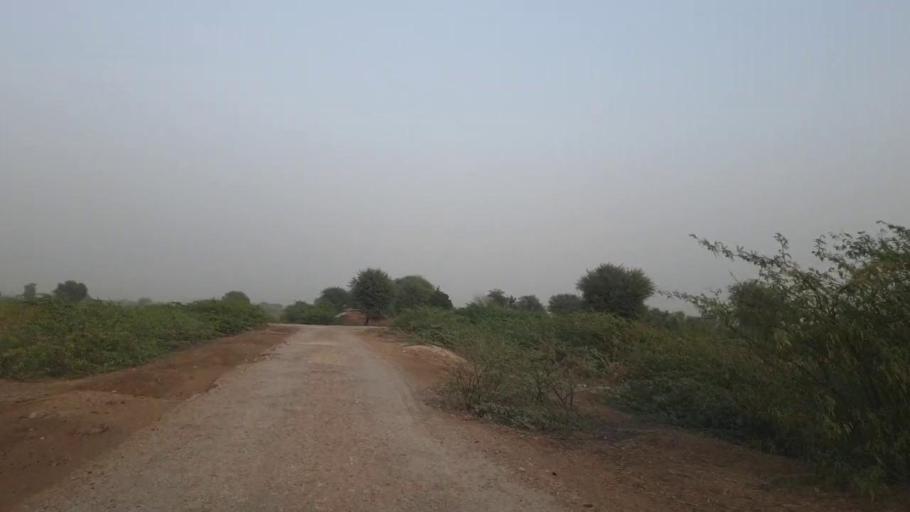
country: PK
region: Sindh
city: Kunri
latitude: 25.1193
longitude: 69.5544
